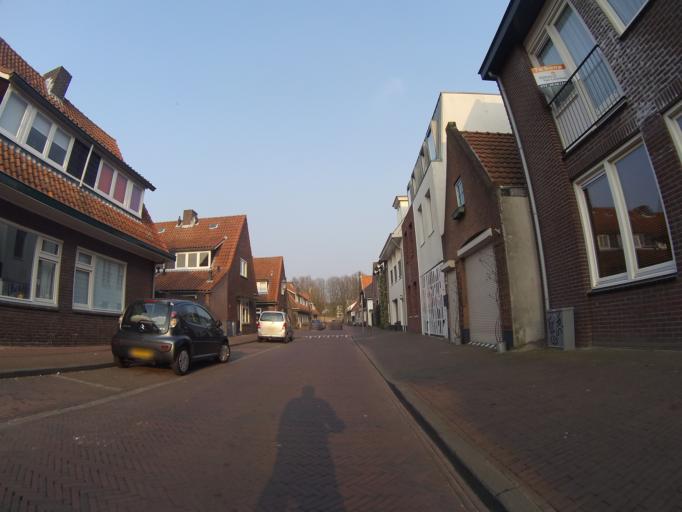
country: NL
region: Utrecht
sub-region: Gemeente Amersfoort
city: Amersfoort
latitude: 52.1586
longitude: 5.3949
